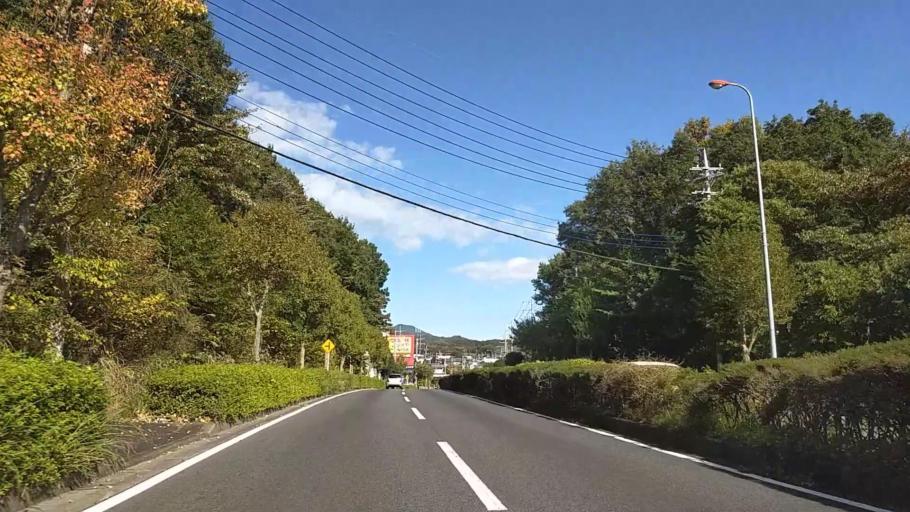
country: JP
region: Kanagawa
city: Hadano
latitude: 35.3448
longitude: 139.2311
